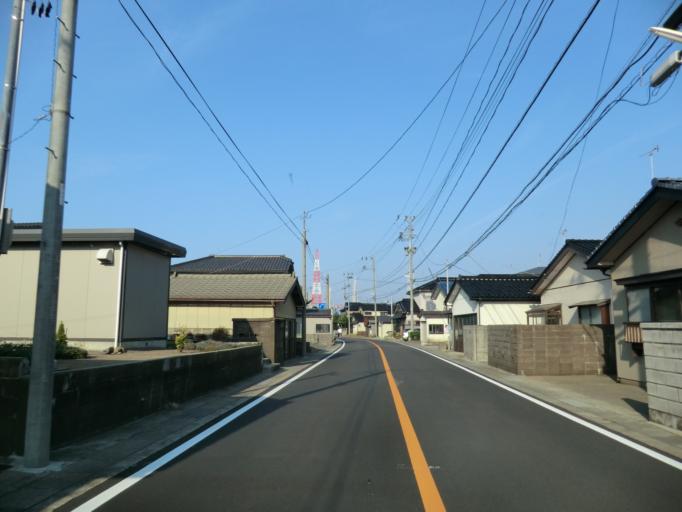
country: JP
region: Niigata
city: Kashiwazaki
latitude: 37.4156
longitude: 138.5856
